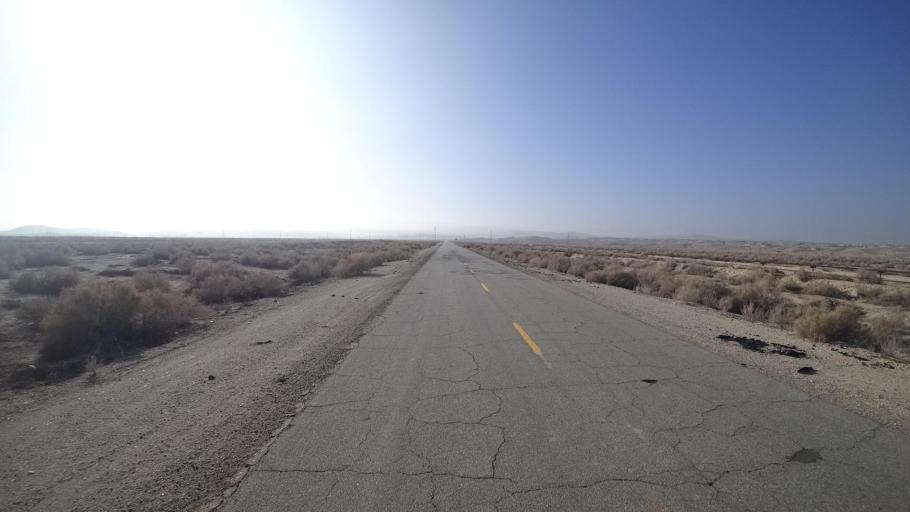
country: US
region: California
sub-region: Kern County
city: Maricopa
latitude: 35.0999
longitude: -119.3984
